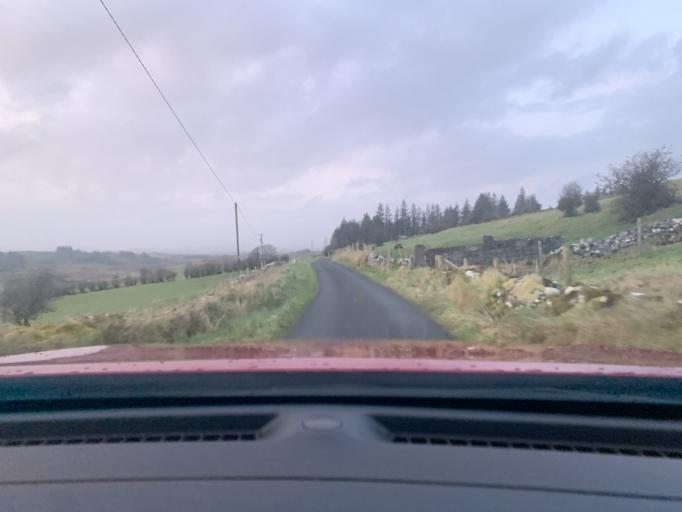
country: IE
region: Connaught
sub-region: Sligo
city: Ballymote
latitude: 54.0560
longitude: -8.3964
